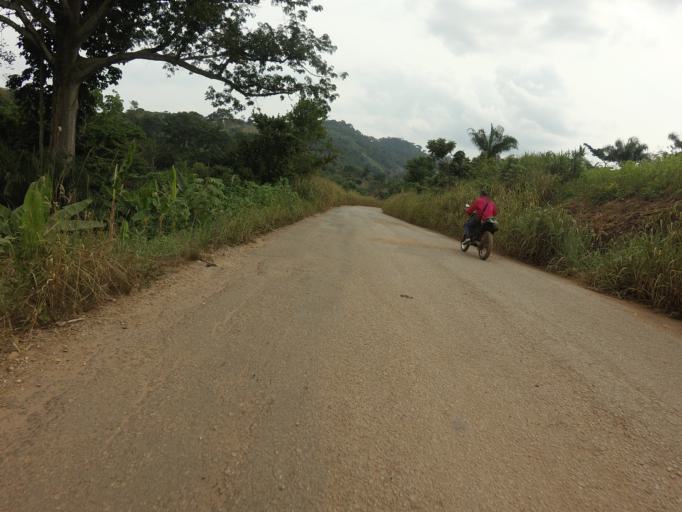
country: GH
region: Volta
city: Ho
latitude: 6.6858
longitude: 0.3474
